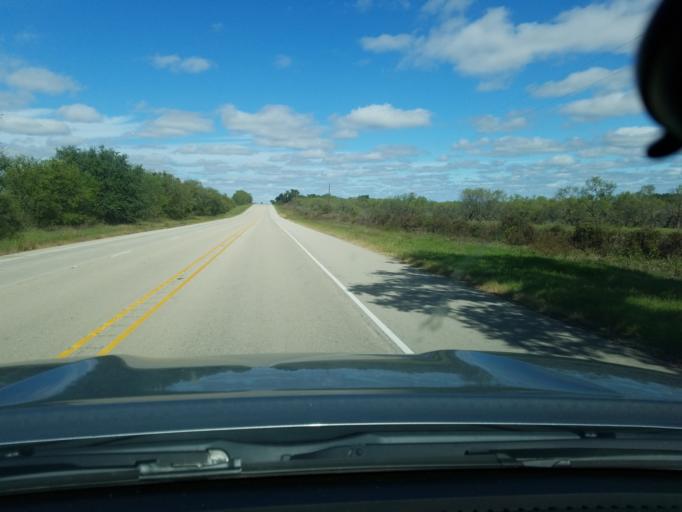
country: US
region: Texas
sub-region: Hamilton County
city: Hamilton
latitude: 31.5642
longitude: -98.1587
